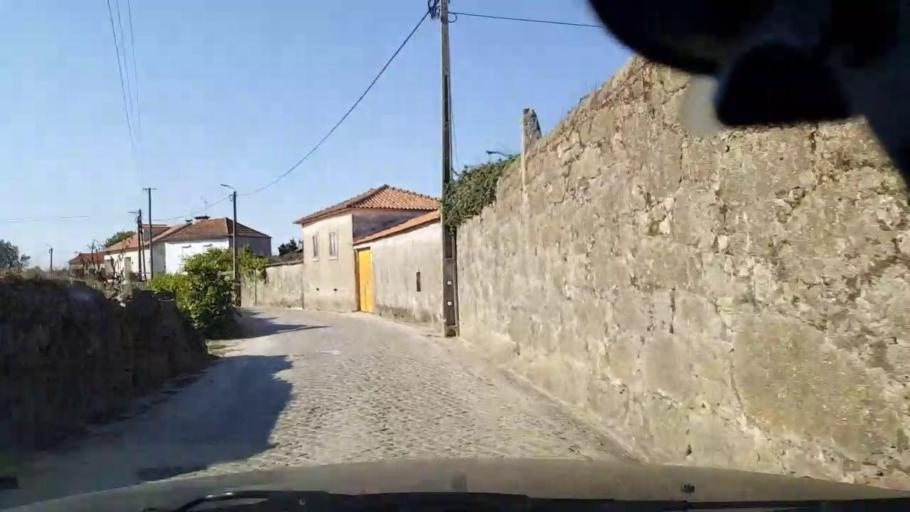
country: PT
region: Porto
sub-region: Vila do Conde
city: Arvore
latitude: 41.3591
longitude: -8.7200
